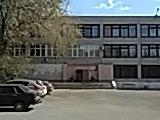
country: RU
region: Orenburg
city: Novotroitsk
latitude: 51.1851
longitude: 58.2808
